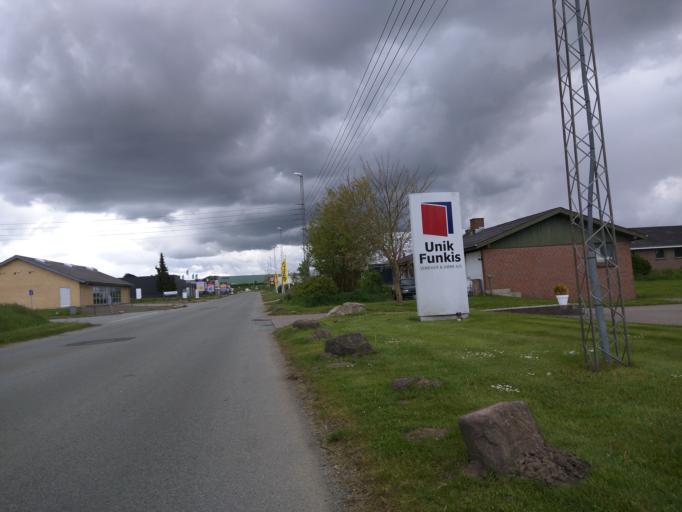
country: DK
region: Central Jutland
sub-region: Viborg Kommune
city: Viborg
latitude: 56.4517
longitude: 9.3683
